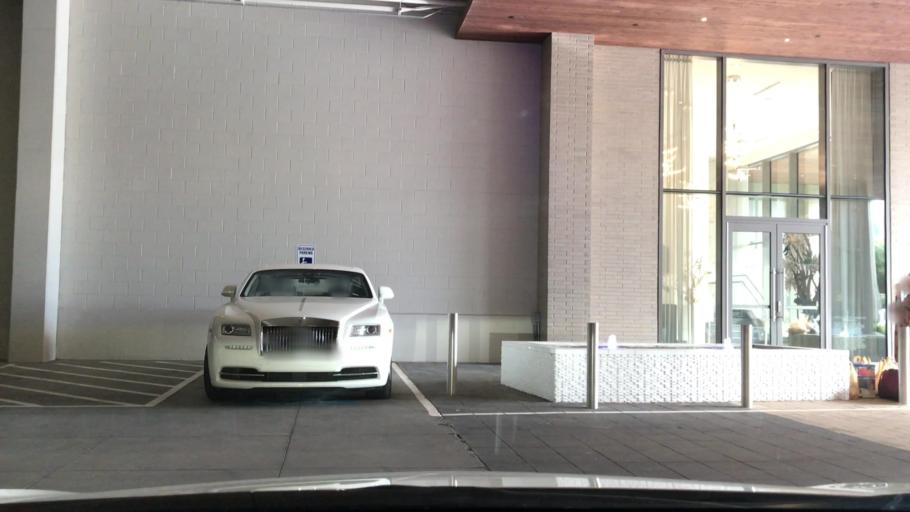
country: US
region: Texas
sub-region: Dallas County
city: Dallas
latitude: 32.7866
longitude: -96.8101
